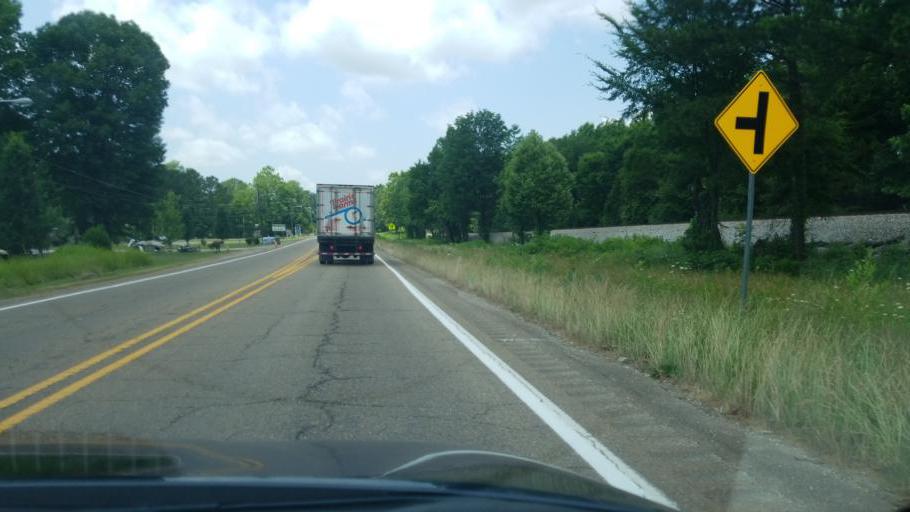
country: US
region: Tennessee
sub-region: Carroll County
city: Huntingdon
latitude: 36.0147
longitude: -88.3843
